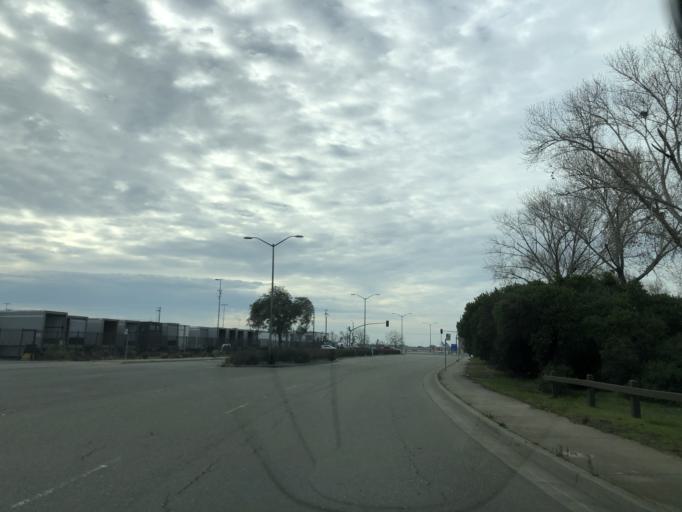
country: US
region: California
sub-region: Alameda County
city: Alameda
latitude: 37.7309
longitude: -122.2067
